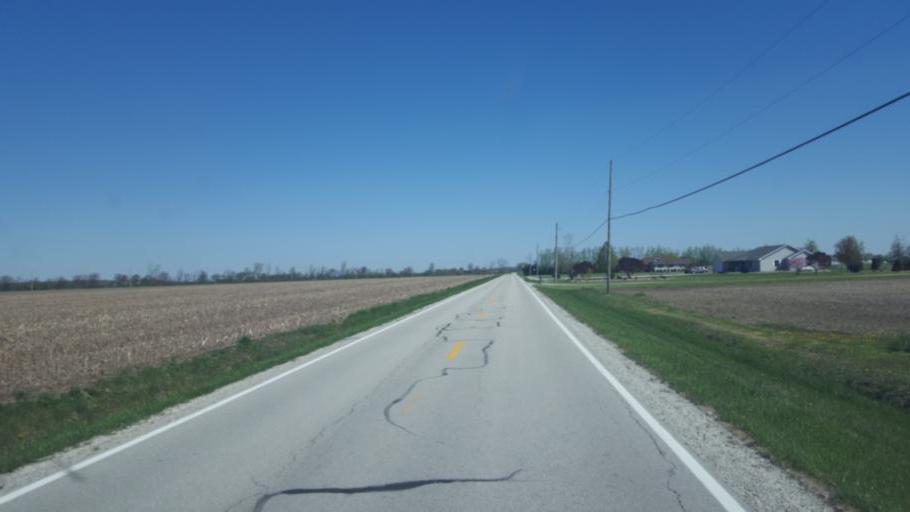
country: US
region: Ohio
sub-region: Sandusky County
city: Stony Prairie
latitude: 41.2942
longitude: -83.1974
